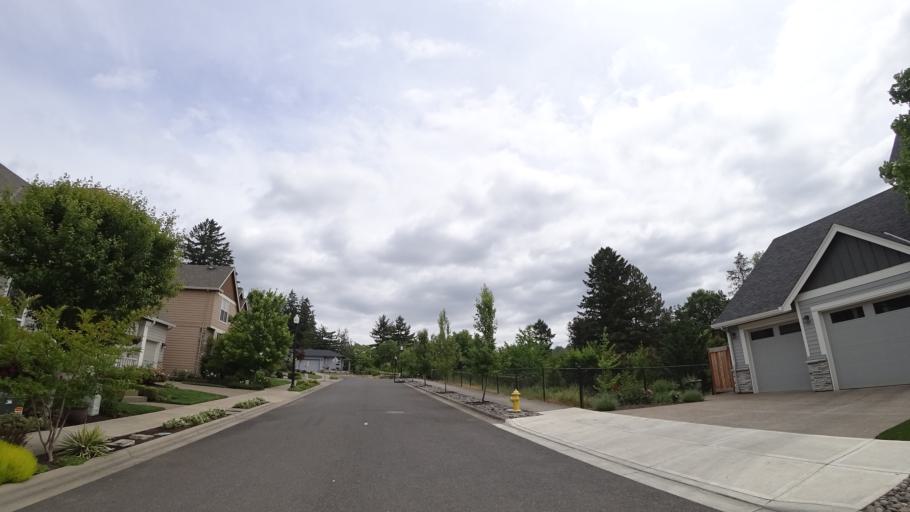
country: US
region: Oregon
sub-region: Washington County
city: Garden Home-Whitford
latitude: 45.4618
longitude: -122.7536
